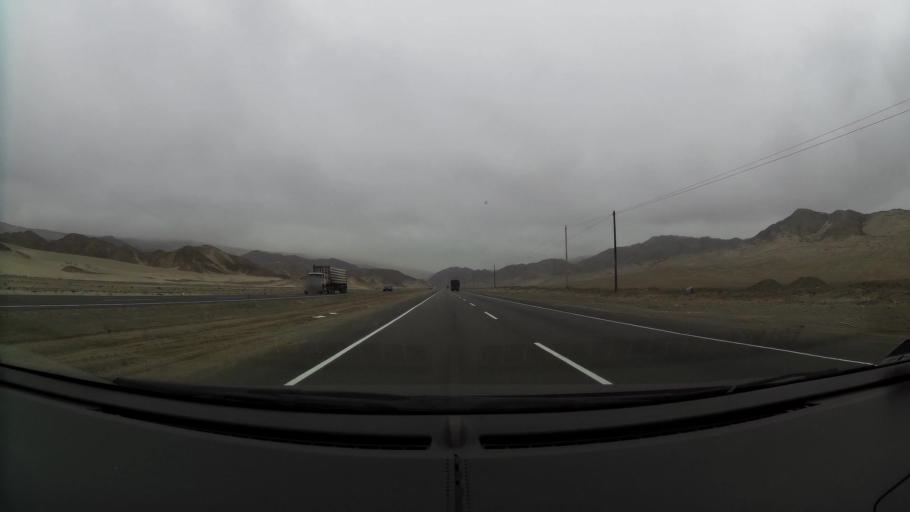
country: PE
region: La Libertad
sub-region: Viru
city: Chao
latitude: -8.7293
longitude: -78.6357
